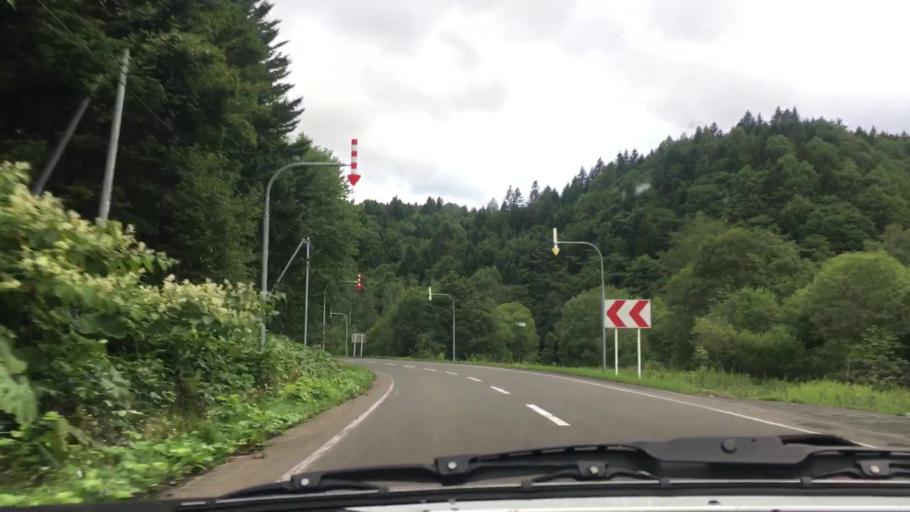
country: JP
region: Hokkaido
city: Shimo-furano
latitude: 43.0725
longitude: 142.6714
